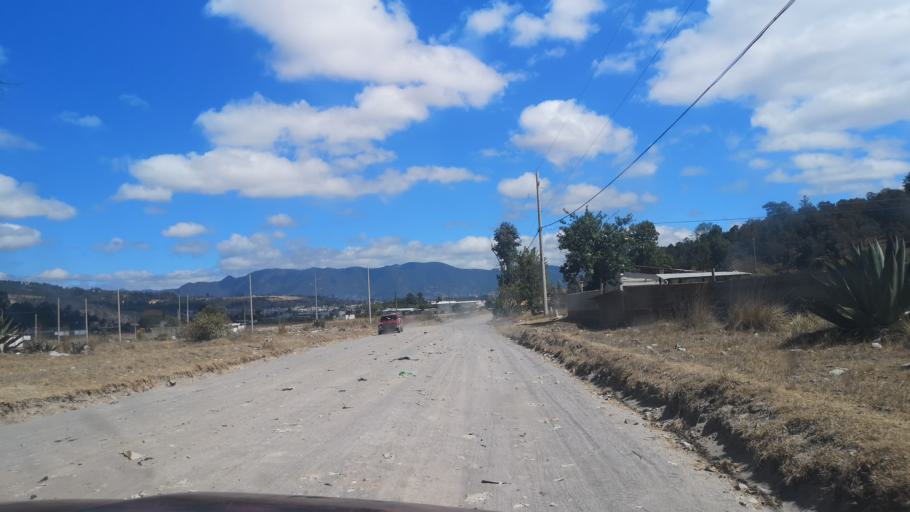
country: GT
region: Quetzaltenango
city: Quetzaltenango
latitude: 14.8096
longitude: -91.5358
